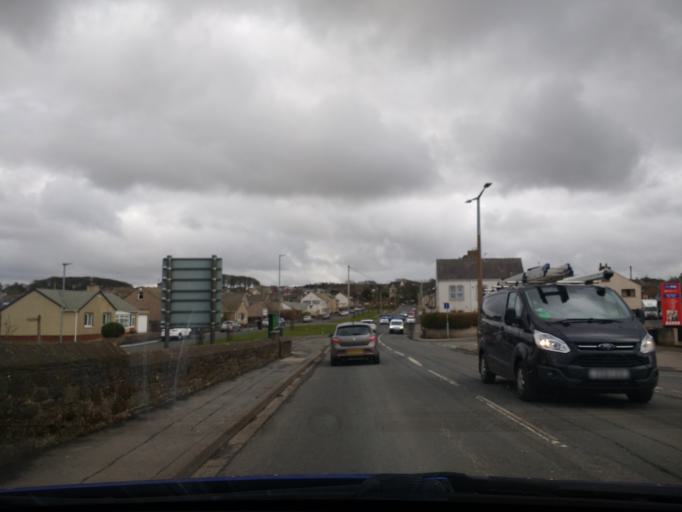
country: GB
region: England
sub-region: Cumbria
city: Maryport
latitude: 54.7127
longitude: -3.4895
